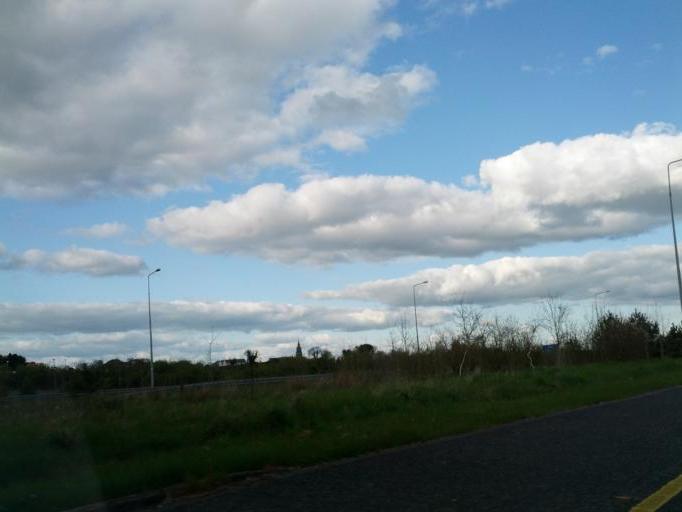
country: IE
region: Leinster
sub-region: An Iarmhi
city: Kinnegad
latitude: 53.4506
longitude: -7.1062
